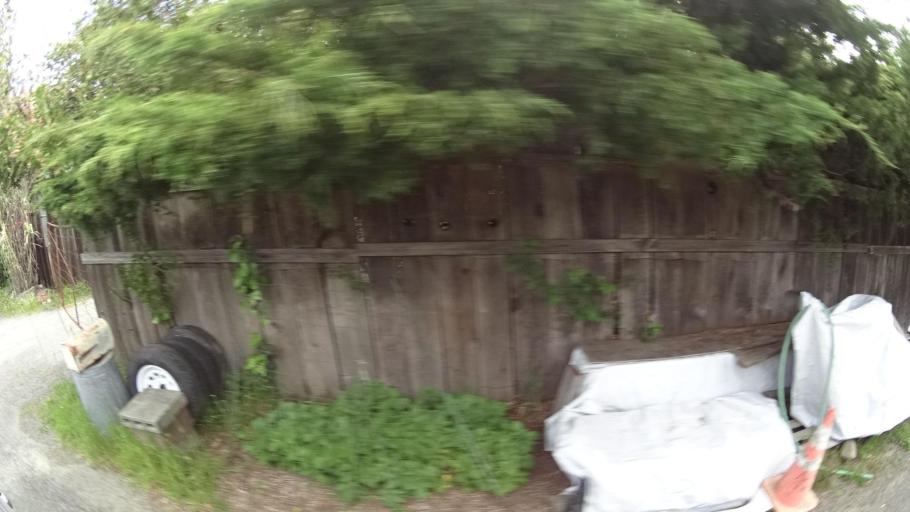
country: US
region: California
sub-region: Humboldt County
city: Redway
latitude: 40.0821
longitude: -123.8148
